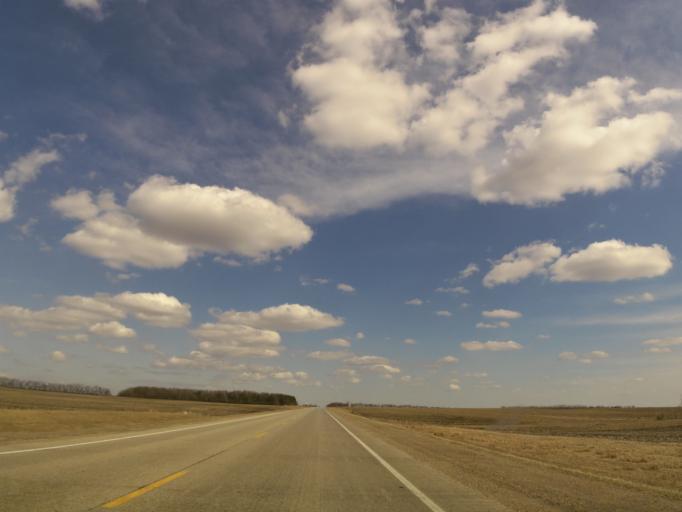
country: US
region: South Dakota
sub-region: Codington County
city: Watertown
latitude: 44.8900
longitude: -96.8941
